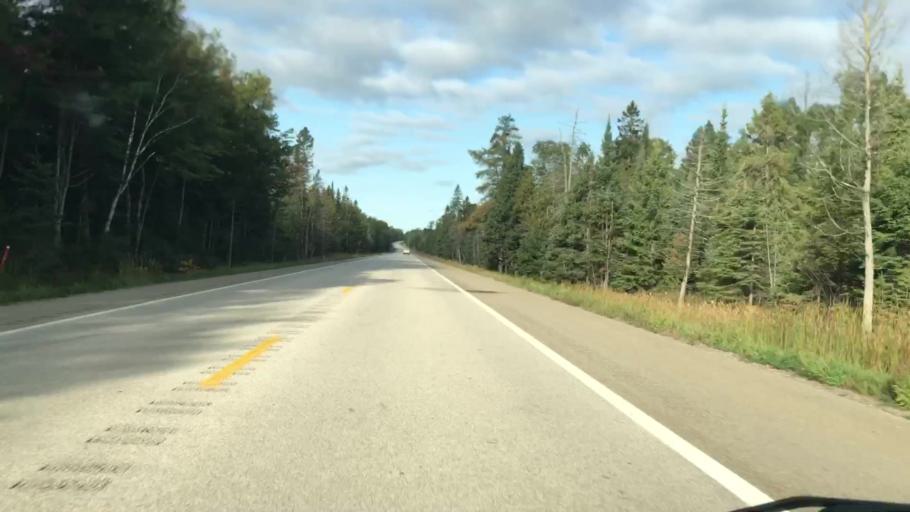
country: US
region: Michigan
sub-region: Luce County
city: Newberry
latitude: 46.3319
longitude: -85.0655
